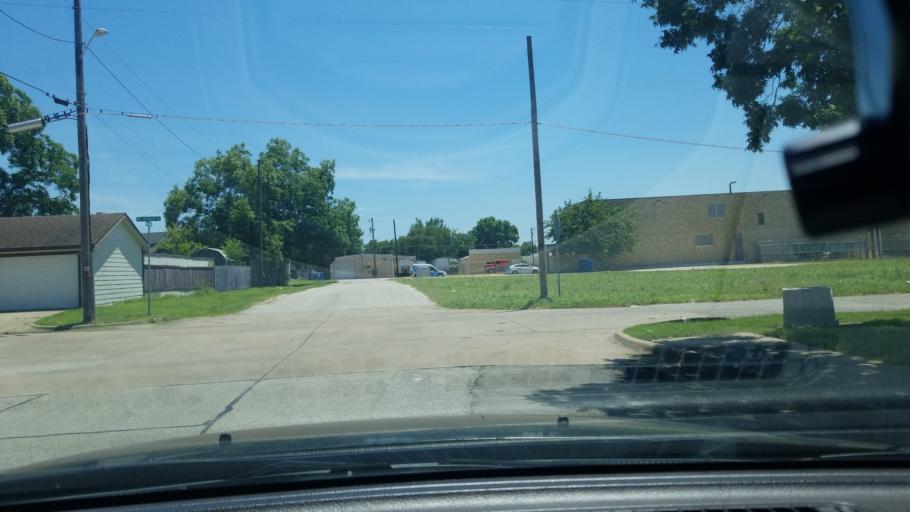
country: US
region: Texas
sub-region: Dallas County
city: Mesquite
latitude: 32.7700
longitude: -96.6009
